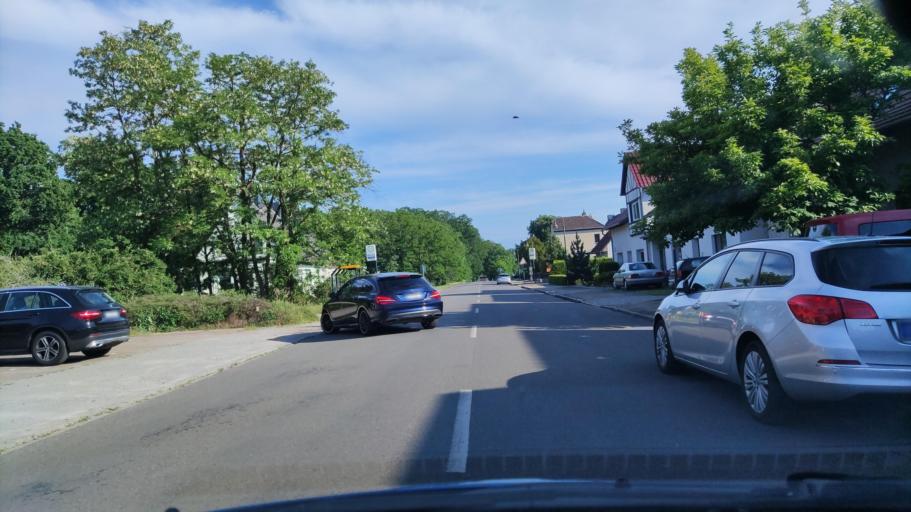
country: DE
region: Saxony-Anhalt
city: Gardelegen
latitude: 52.5137
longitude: 11.4001
